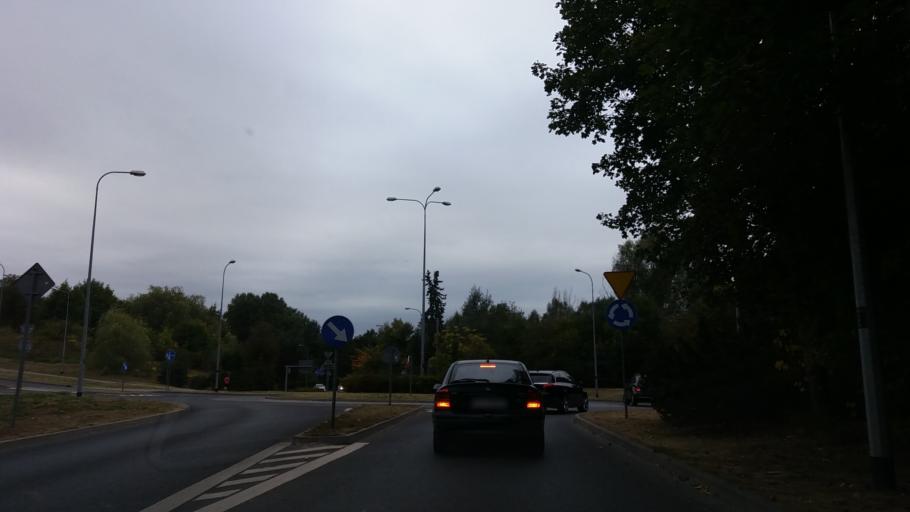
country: PL
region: Lubusz
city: Gorzow Wielkopolski
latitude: 52.7619
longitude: 15.2310
